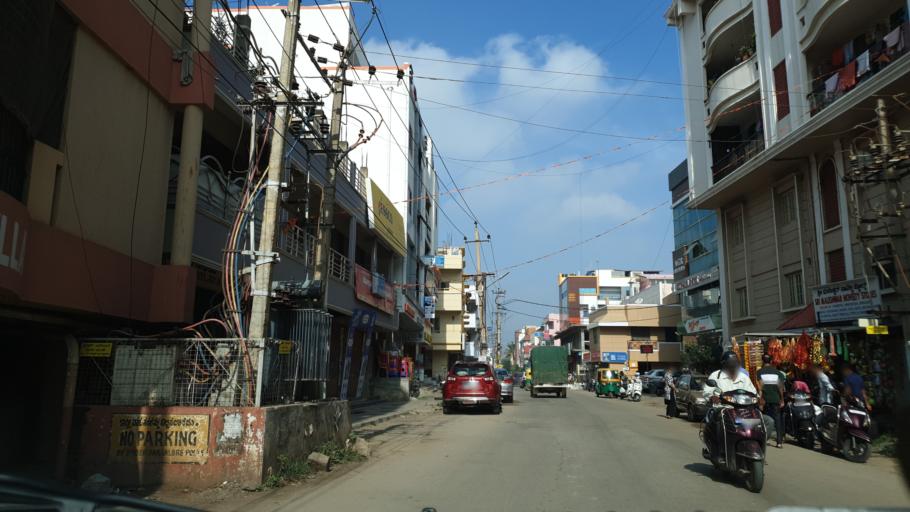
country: IN
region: Karnataka
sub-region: Bangalore Urban
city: Bangalore
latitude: 12.9723
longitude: 77.6796
